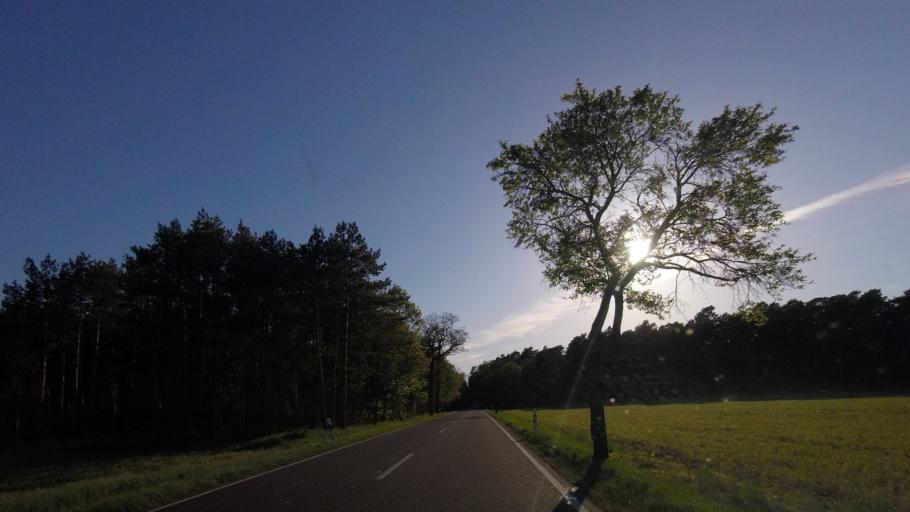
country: DE
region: Brandenburg
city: Baruth
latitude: 51.9963
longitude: 13.3990
